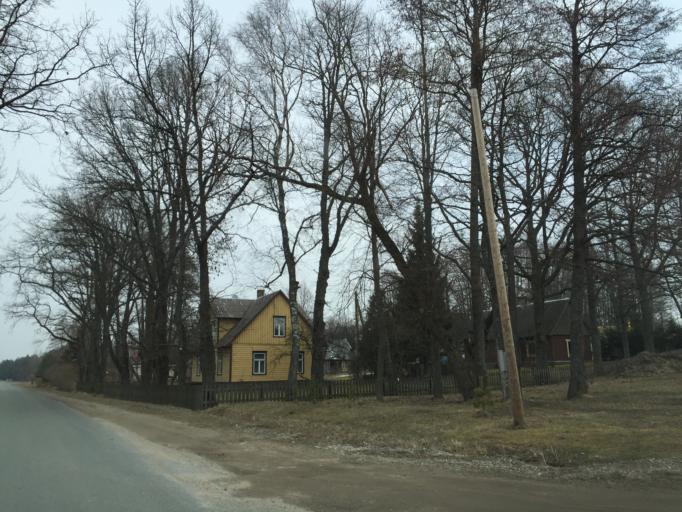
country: LV
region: Salacgrivas
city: Ainazi
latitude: 58.0070
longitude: 24.4460
